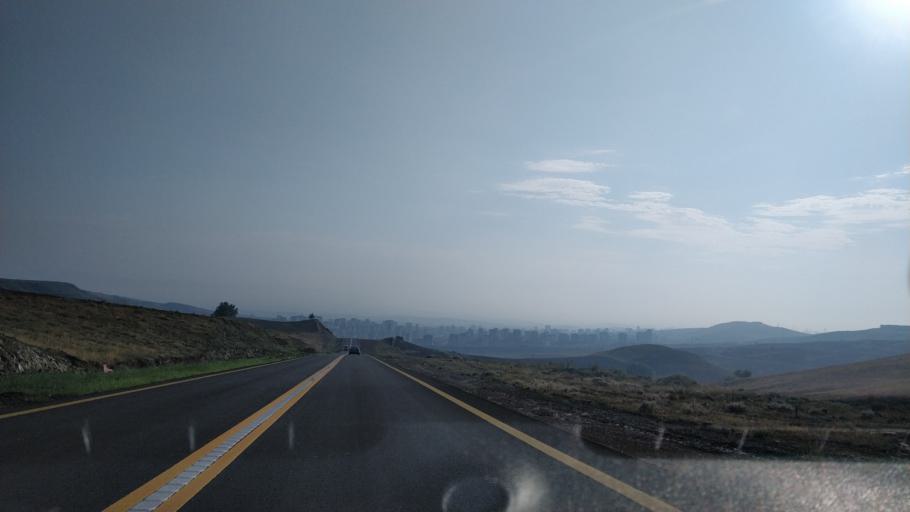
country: TR
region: Ankara
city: Etimesgut
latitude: 39.8717
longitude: 32.5930
